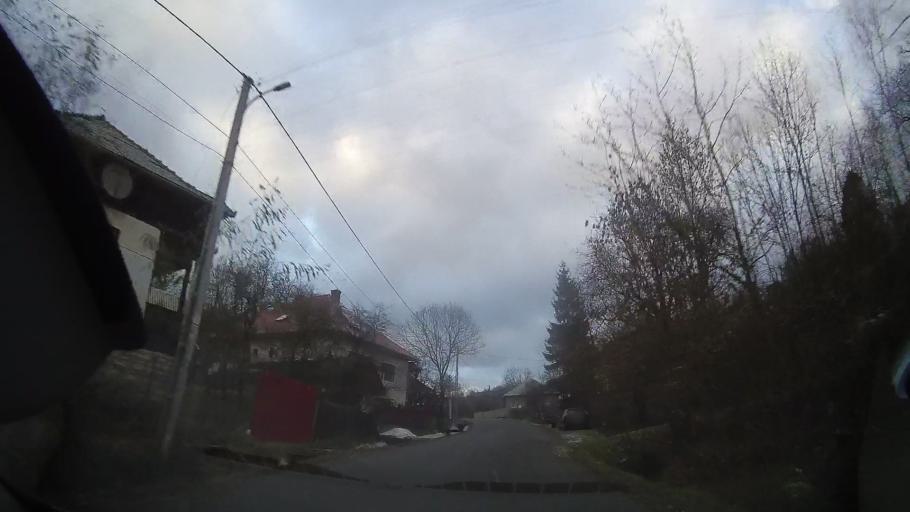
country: RO
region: Cluj
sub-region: Comuna Calatele
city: Calatele
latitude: 46.7804
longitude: 23.0412
